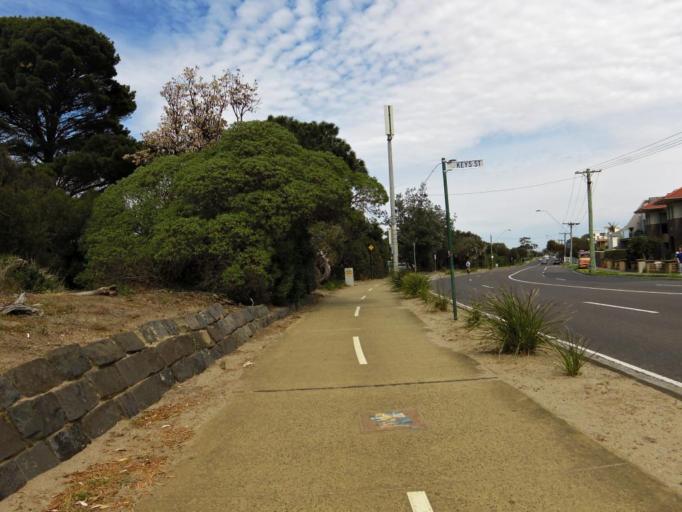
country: AU
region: Victoria
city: Beaumaris
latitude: -37.9921
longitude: 145.0421
